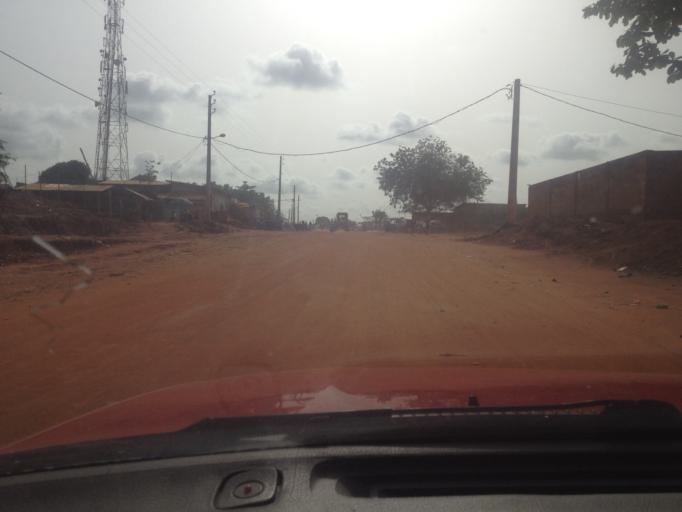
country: BJ
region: Atlantique
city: Abomey-Calavi
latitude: 6.4634
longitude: 2.3041
